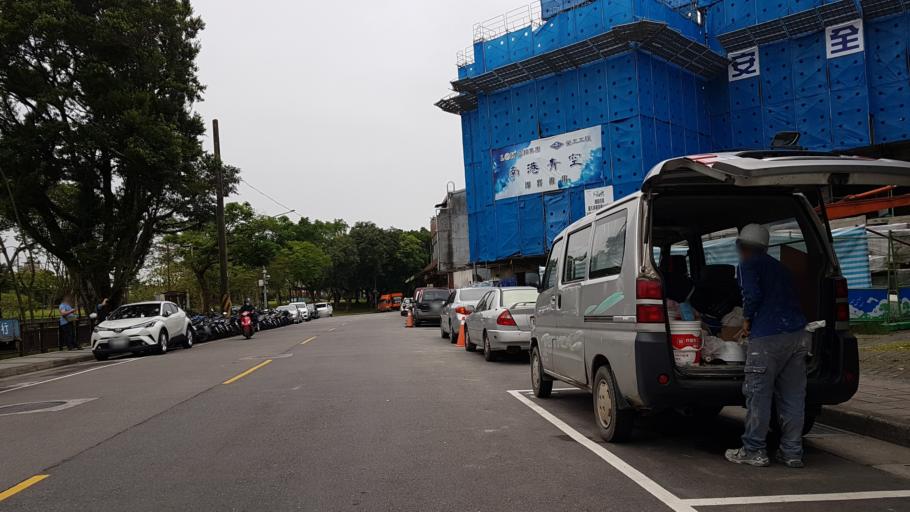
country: TW
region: Taipei
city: Taipei
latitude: 25.0428
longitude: 121.5928
